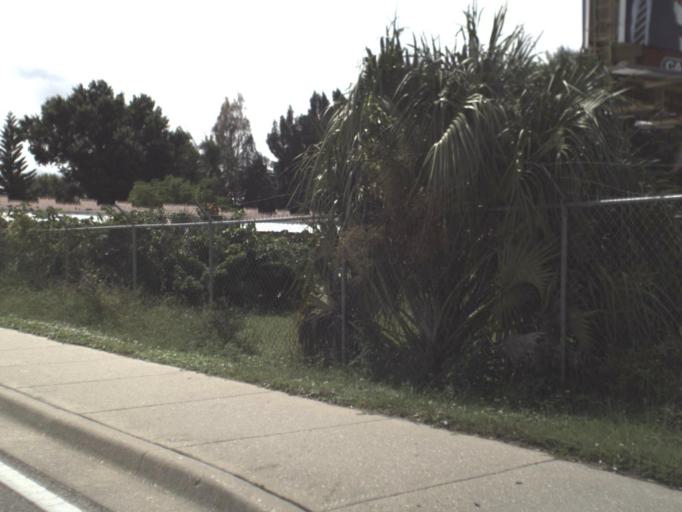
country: US
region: Florida
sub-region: Lee County
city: North Fort Myers
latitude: 26.6727
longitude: -81.8832
